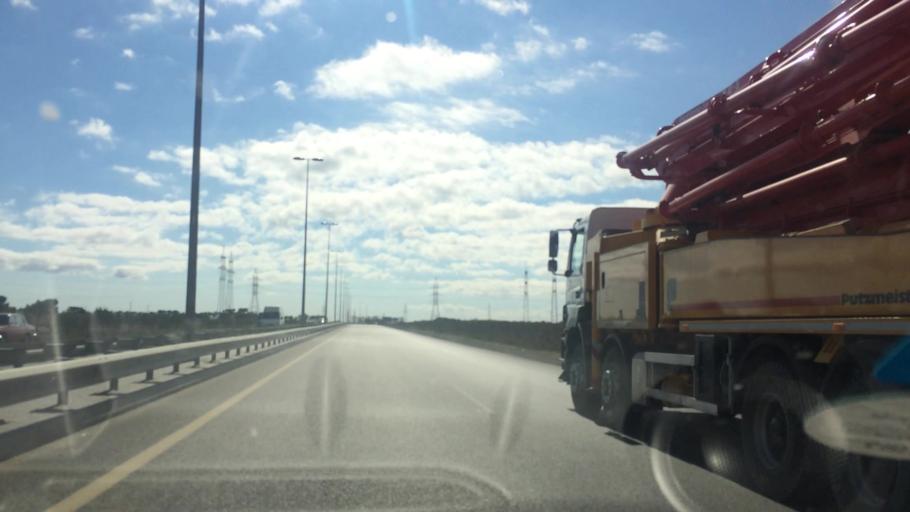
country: AZ
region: Baki
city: Qala
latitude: 40.4404
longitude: 50.1814
